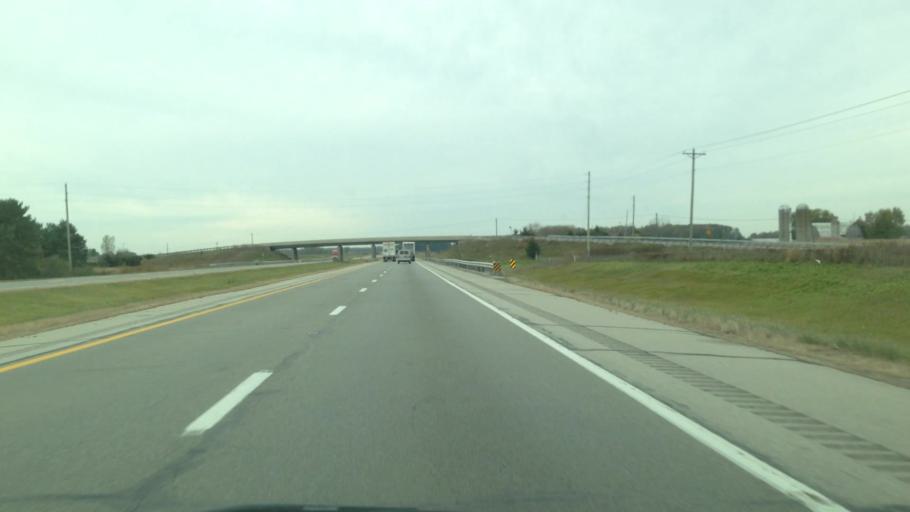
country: US
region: Ohio
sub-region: Williams County
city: Montpelier
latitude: 41.6215
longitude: -84.6887
